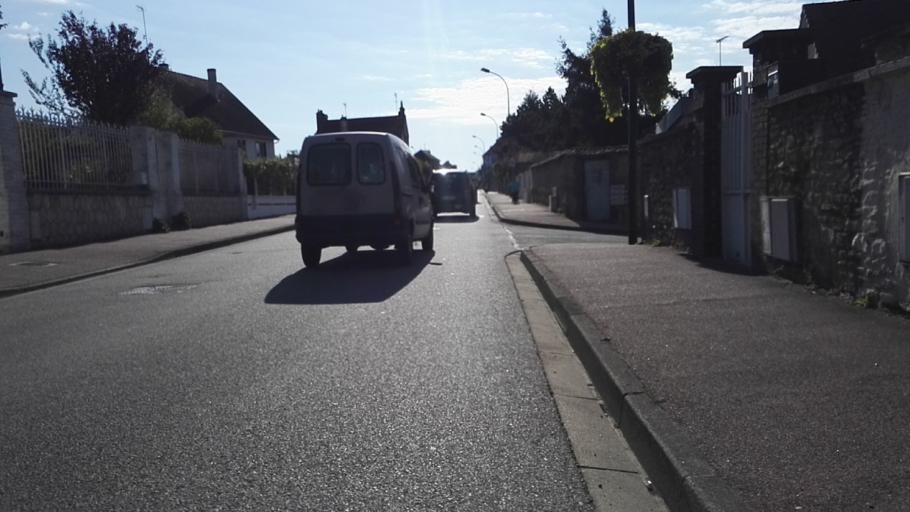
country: FR
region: Haute-Normandie
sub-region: Departement de l'Eure
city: Pacy-sur-Eure
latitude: 49.0178
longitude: 1.3819
